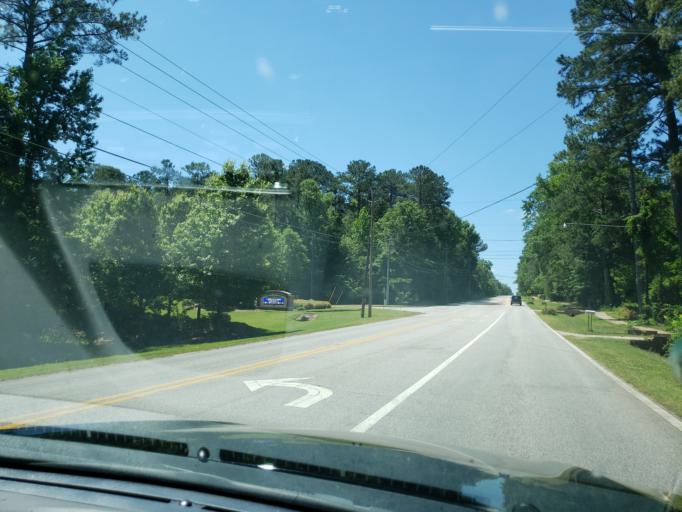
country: US
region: Alabama
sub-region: Lee County
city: Auburn
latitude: 32.6282
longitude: -85.4819
